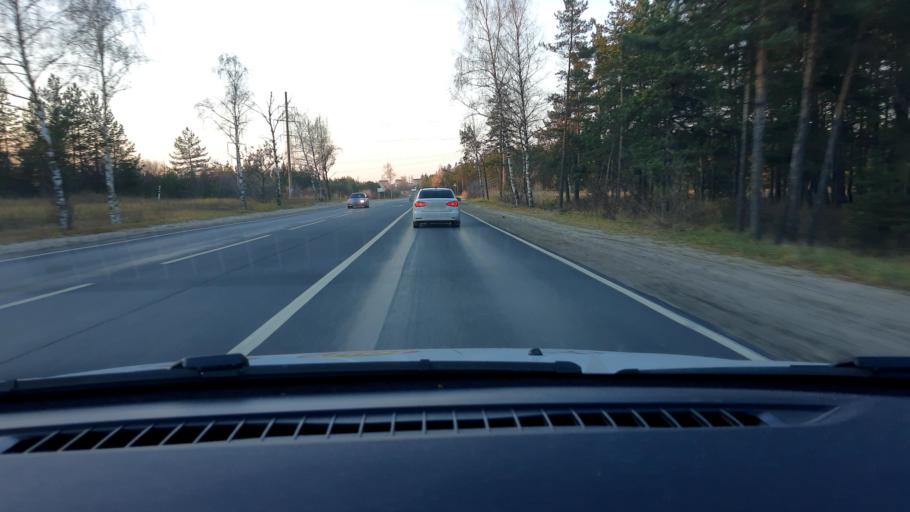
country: RU
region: Nizjnij Novgorod
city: Dzerzhinsk
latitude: 56.2684
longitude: 43.4717
